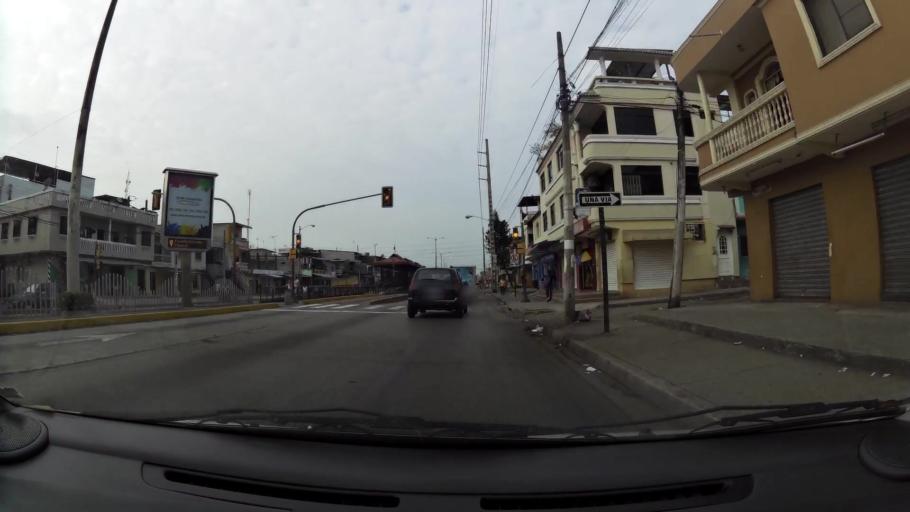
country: EC
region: Guayas
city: Guayaquil
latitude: -2.2497
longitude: -79.8903
